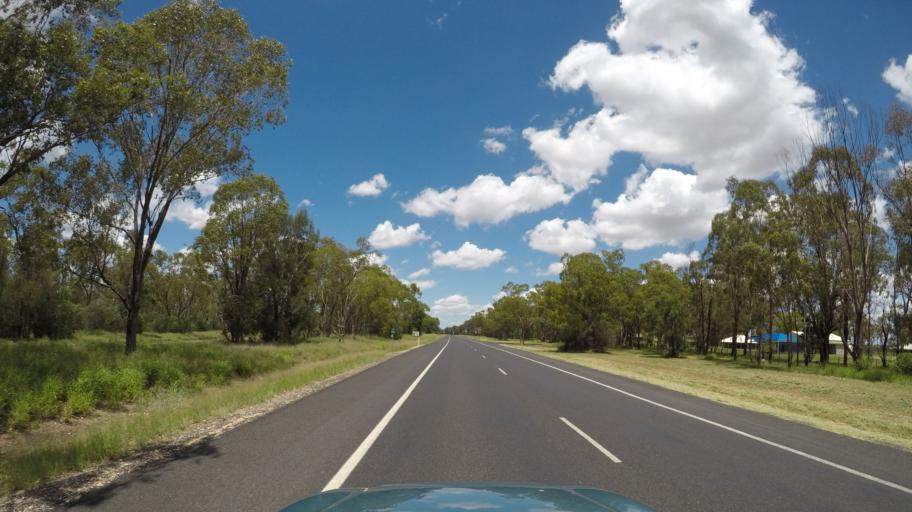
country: AU
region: Queensland
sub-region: Goondiwindi
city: Goondiwindi
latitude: -28.0794
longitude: 150.7410
